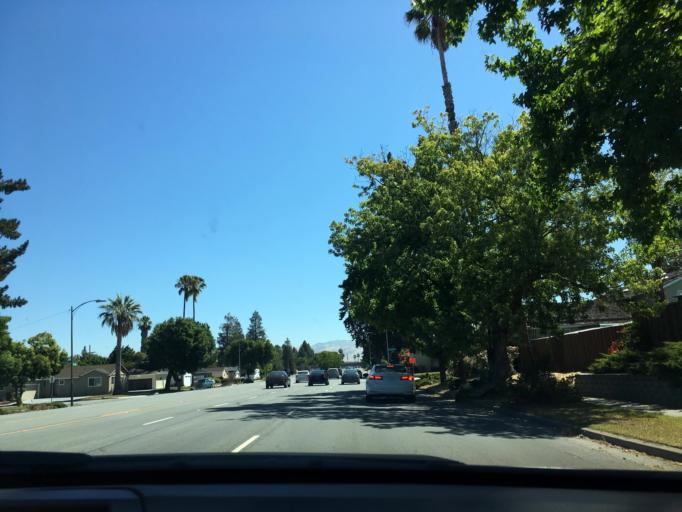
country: US
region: California
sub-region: Santa Clara County
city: Seven Trees
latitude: 37.2740
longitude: -121.8835
